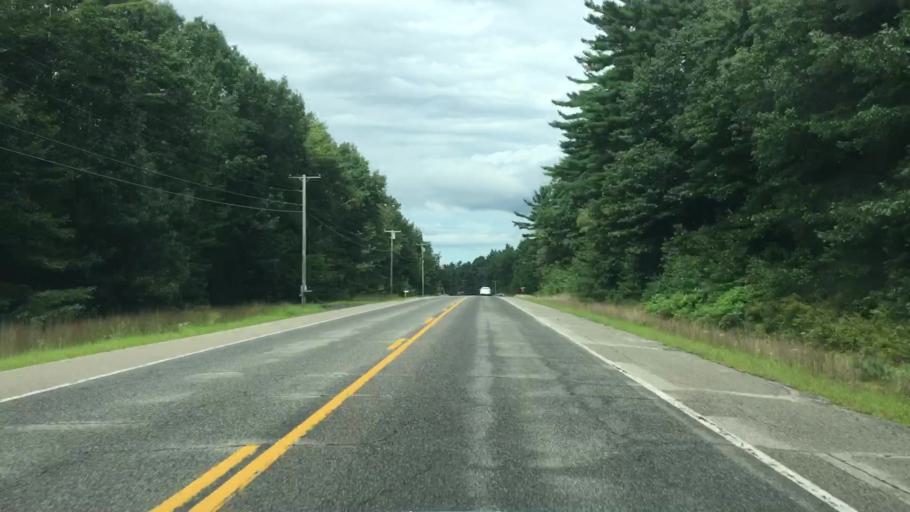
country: US
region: Maine
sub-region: York County
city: South Sanford
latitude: 43.3683
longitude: -70.7329
